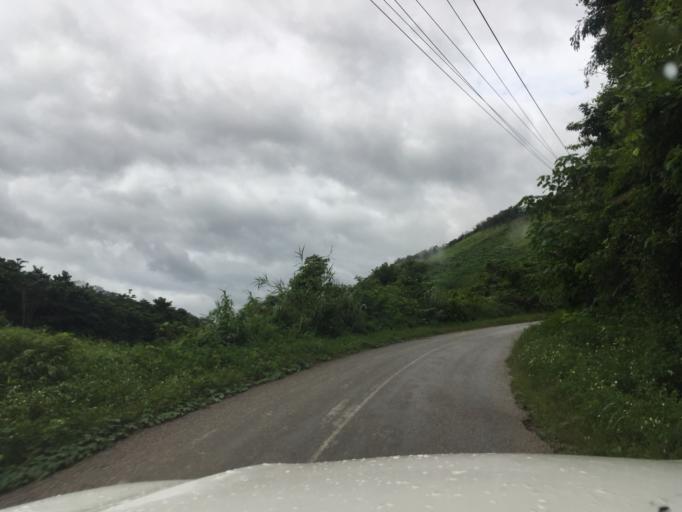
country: LA
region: Oudomxai
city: Muang La
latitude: 21.0058
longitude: 102.2342
